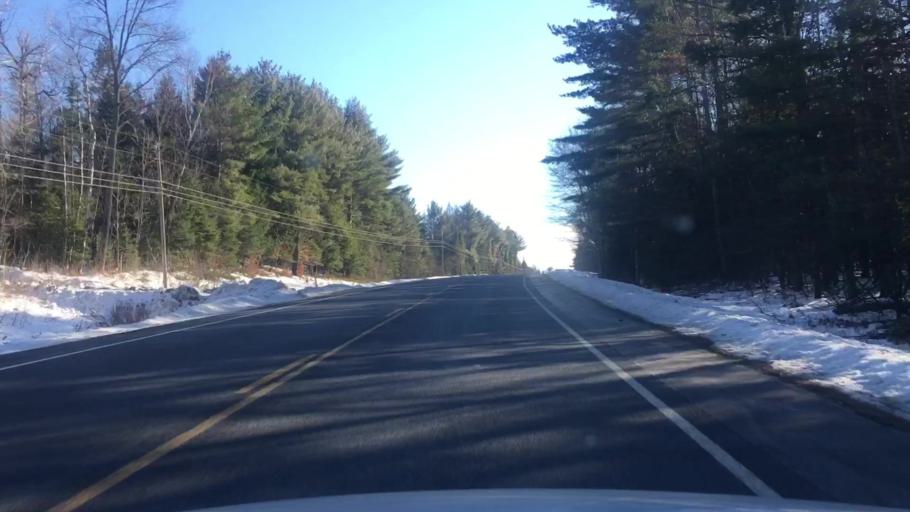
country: US
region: Maine
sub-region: Somerset County
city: Madison
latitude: 44.9224
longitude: -69.8269
